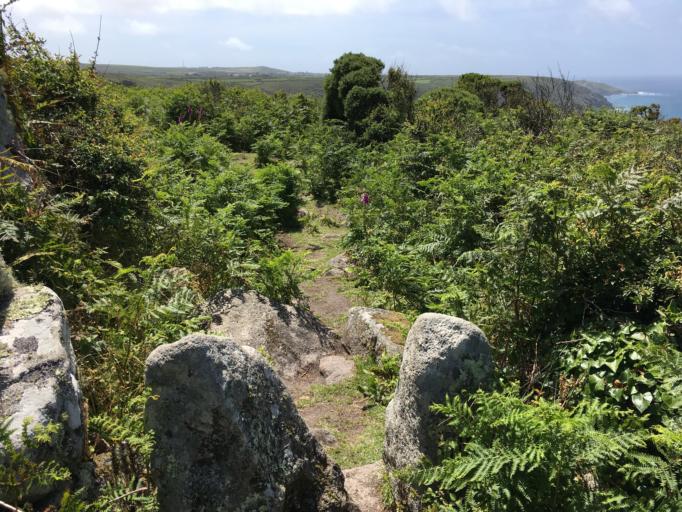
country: GB
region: England
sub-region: Cornwall
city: Saint Just
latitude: 50.1716
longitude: -5.6225
